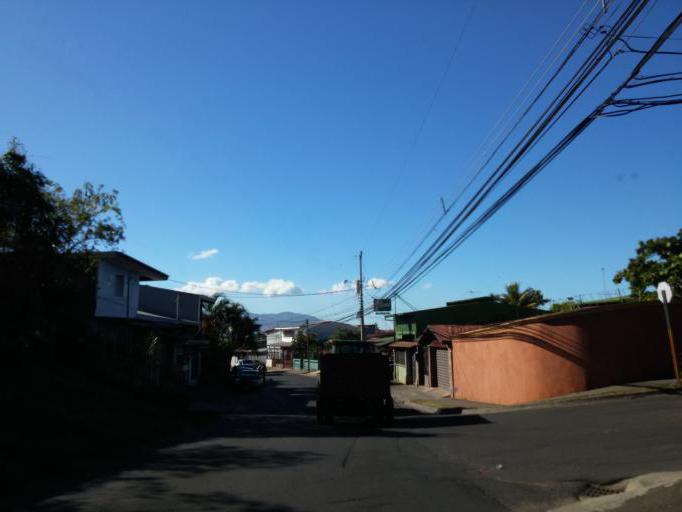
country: CR
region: Alajuela
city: Alajuela
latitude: 10.0326
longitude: -84.2042
